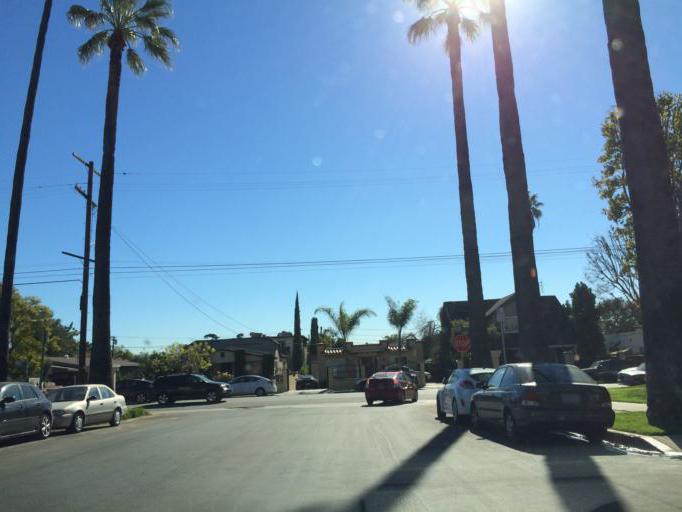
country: US
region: California
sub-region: Los Angeles County
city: Silver Lake
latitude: 34.1058
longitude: -118.2889
